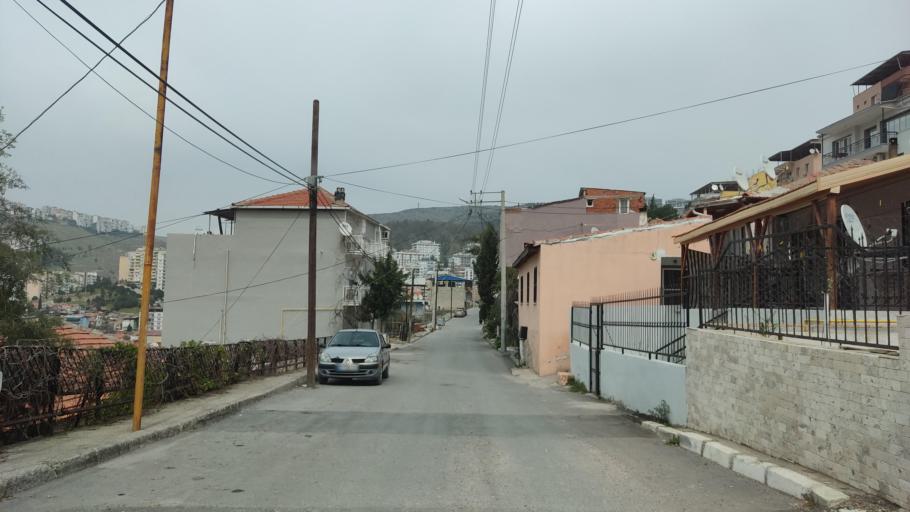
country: TR
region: Izmir
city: Karsiyaka
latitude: 38.4980
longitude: 27.0715
